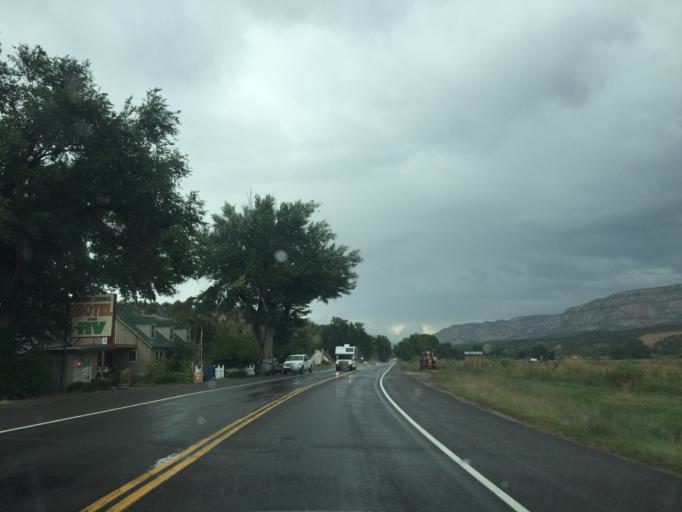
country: US
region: Utah
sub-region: Kane County
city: Kanab
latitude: 37.2416
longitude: -112.6711
